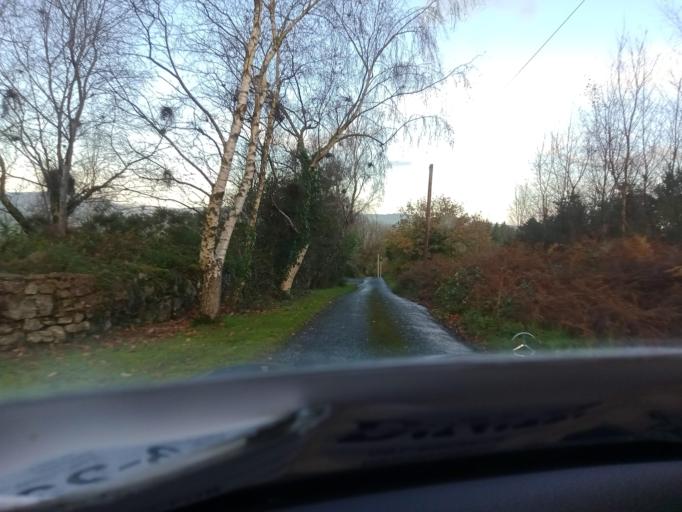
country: IE
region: Munster
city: Carrick-on-Suir
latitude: 52.3348
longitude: -7.4083
